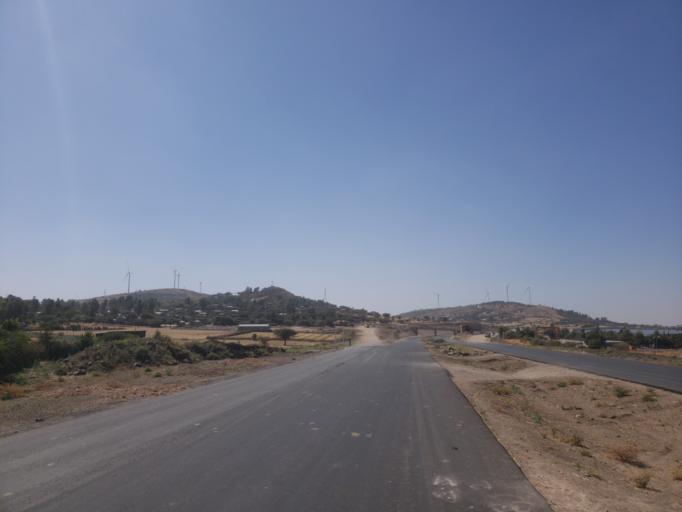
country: ET
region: Oromiya
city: Mojo
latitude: 8.5719
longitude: 39.1679
